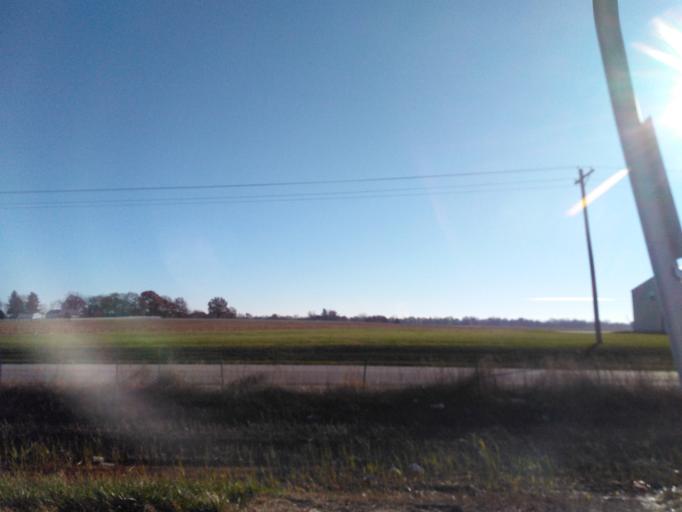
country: US
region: Illinois
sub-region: Madison County
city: Troy
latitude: 38.7415
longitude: -89.9099
